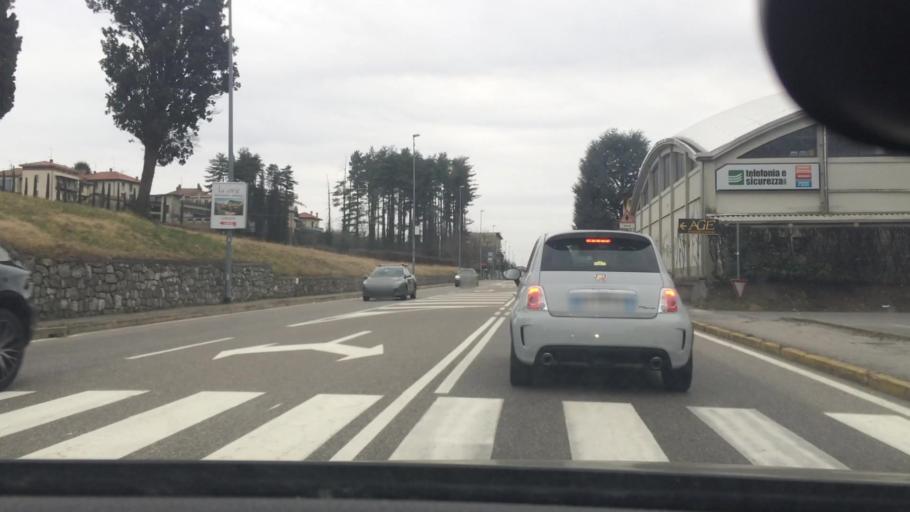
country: IT
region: Lombardy
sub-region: Provincia di Como
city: Lurago d'Erba
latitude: 45.7551
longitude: 9.2241
